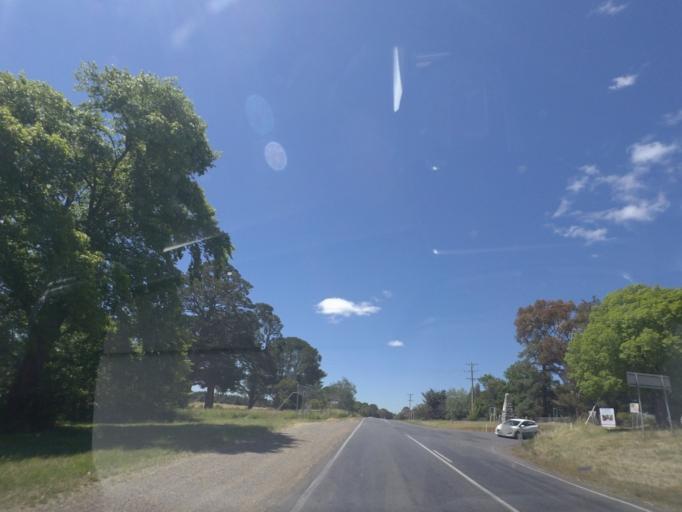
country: AU
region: Victoria
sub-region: Mount Alexander
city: Castlemaine
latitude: -37.2359
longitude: 144.3290
